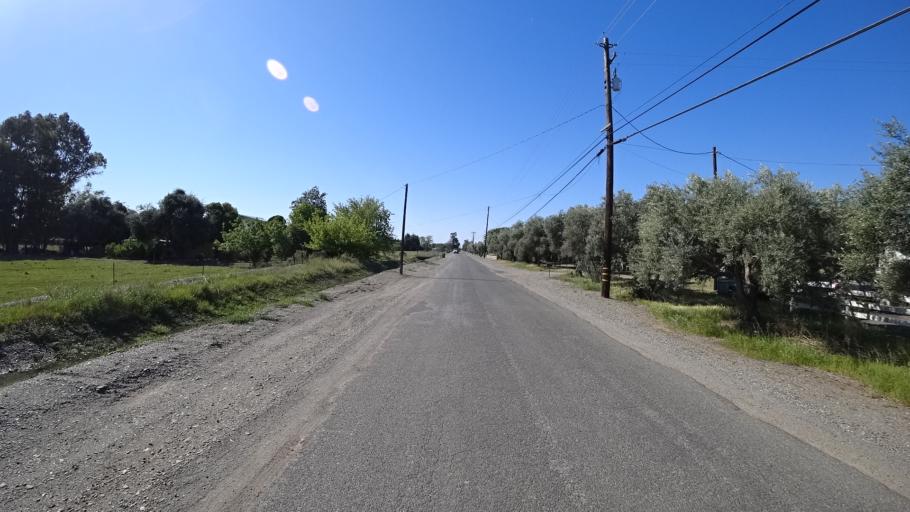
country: US
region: California
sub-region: Glenn County
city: Orland
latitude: 39.7315
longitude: -122.1688
